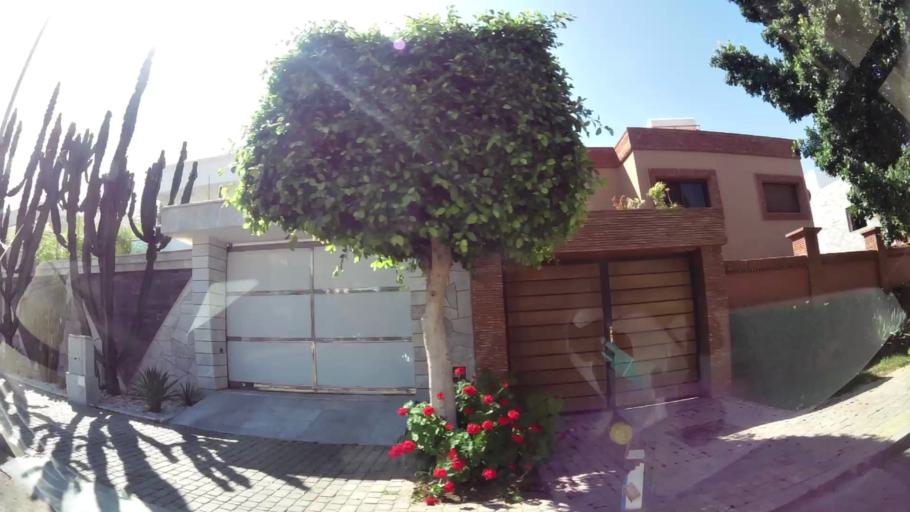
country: MA
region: Souss-Massa-Draa
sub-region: Agadir-Ida-ou-Tnan
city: Agadir
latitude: 30.4385
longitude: -9.5789
